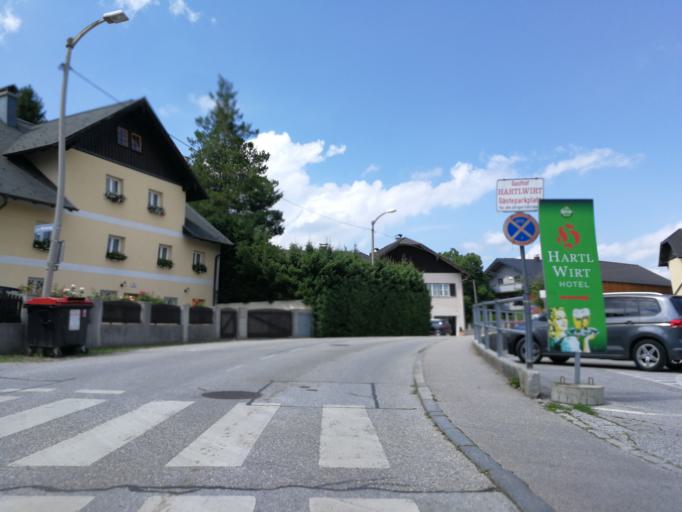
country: AT
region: Salzburg
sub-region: Politischer Bezirk Salzburg-Umgebung
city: Bergheim
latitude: 47.8245
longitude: 13.0092
